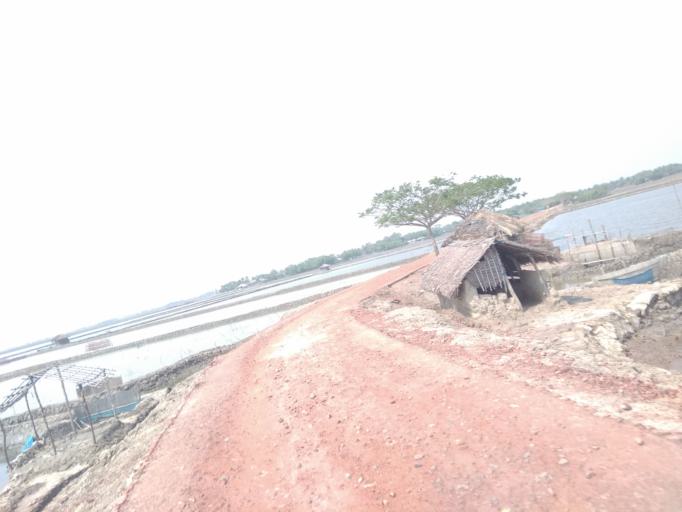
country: IN
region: West Bengal
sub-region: North 24 Parganas
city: Taki
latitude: 22.2927
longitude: 89.2707
